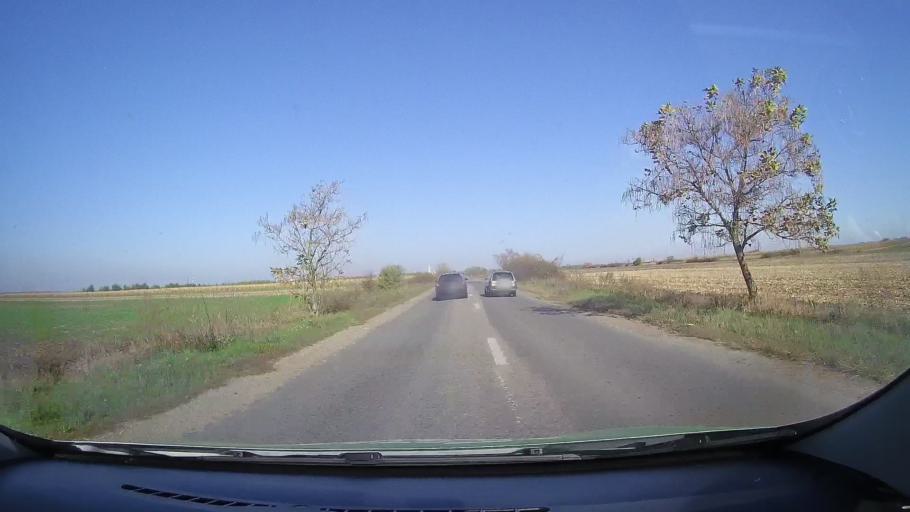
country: RO
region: Satu Mare
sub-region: Comuna Cauas
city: Cauas
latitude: 47.6176
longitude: 22.5353
